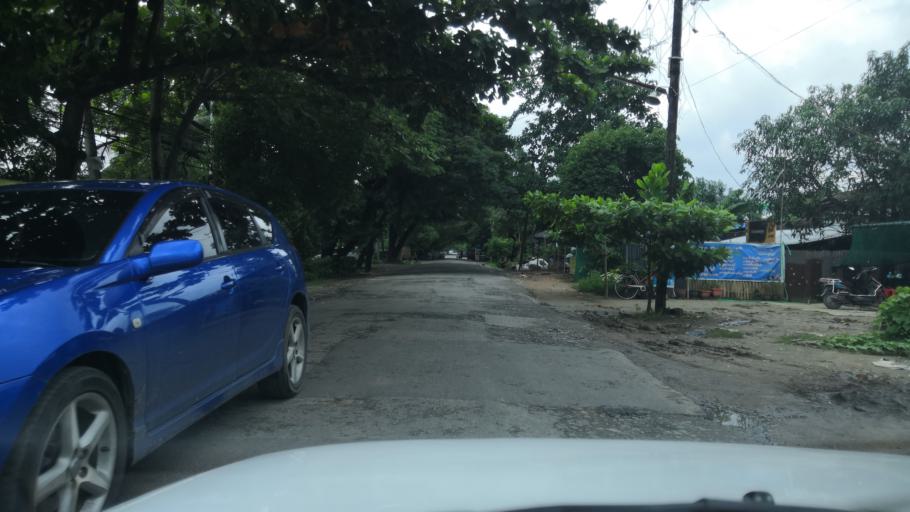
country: MM
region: Yangon
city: Yangon
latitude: 16.8880
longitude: 96.1756
